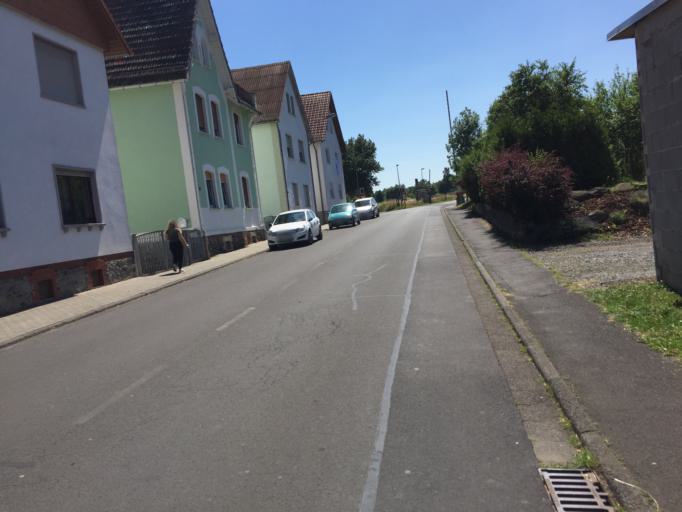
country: DE
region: Hesse
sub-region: Regierungsbezirk Giessen
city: Grossen Buseck
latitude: 50.6043
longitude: 8.7917
